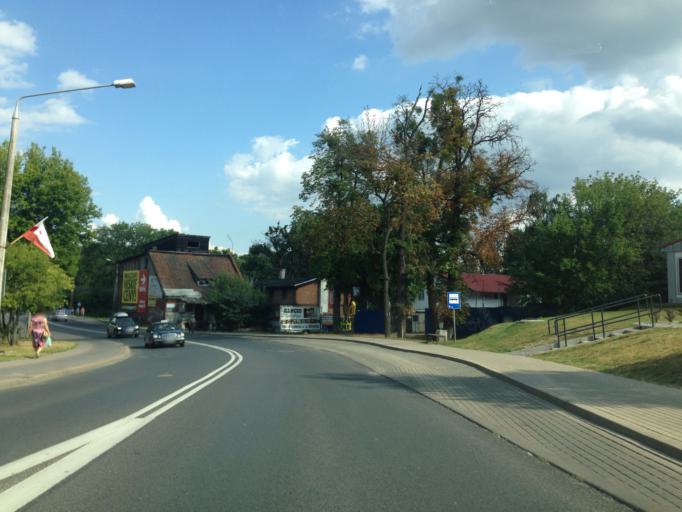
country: PL
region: Warmian-Masurian Voivodeship
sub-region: Powiat ilawski
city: Ilawa
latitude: 53.5948
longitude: 19.5734
